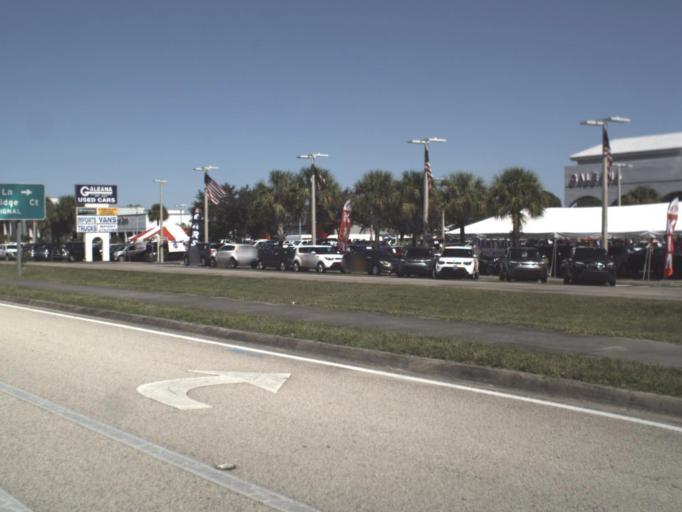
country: US
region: Florida
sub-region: Lee County
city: Villas
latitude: 26.5320
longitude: -81.8711
